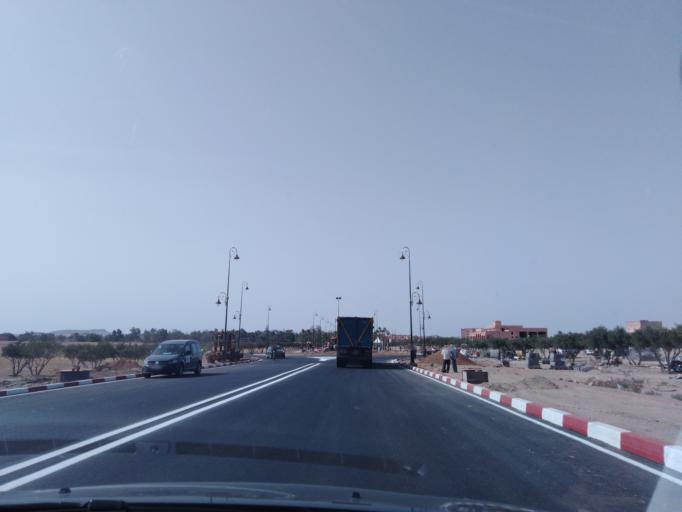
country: MA
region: Marrakech-Tensift-Al Haouz
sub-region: Kelaa-Des-Sraghna
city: Sidi Bou Othmane
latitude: 32.2237
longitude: -7.9572
